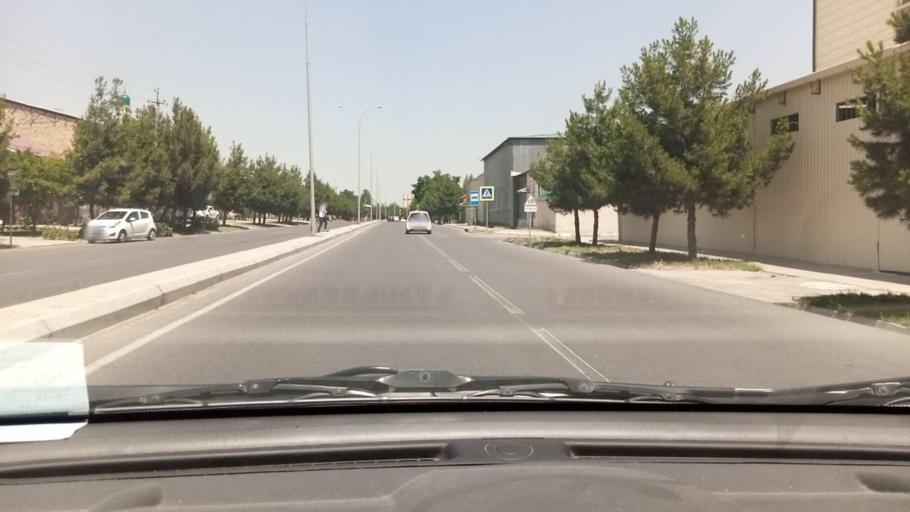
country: UZ
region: Toshkent Shahri
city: Tashkent
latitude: 41.2346
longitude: 69.1876
